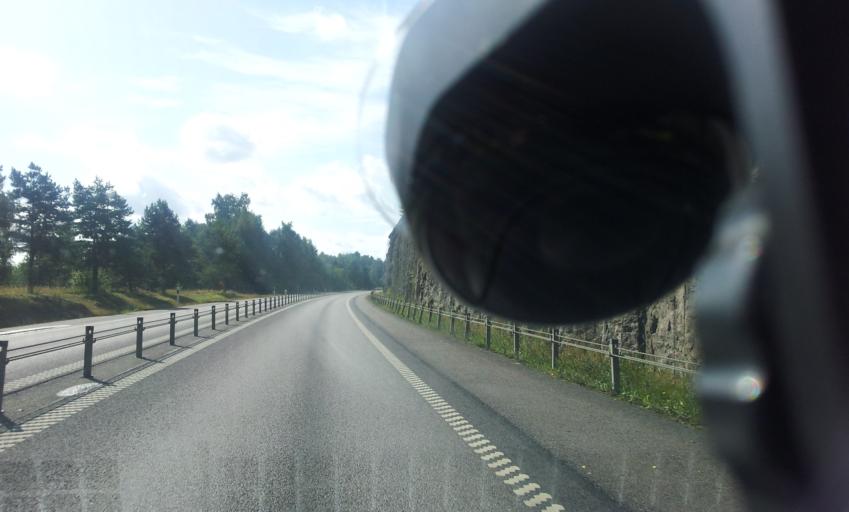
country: SE
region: OEstergoetland
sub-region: Valdemarsviks Kommun
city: Gusum
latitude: 58.3252
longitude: 16.4758
